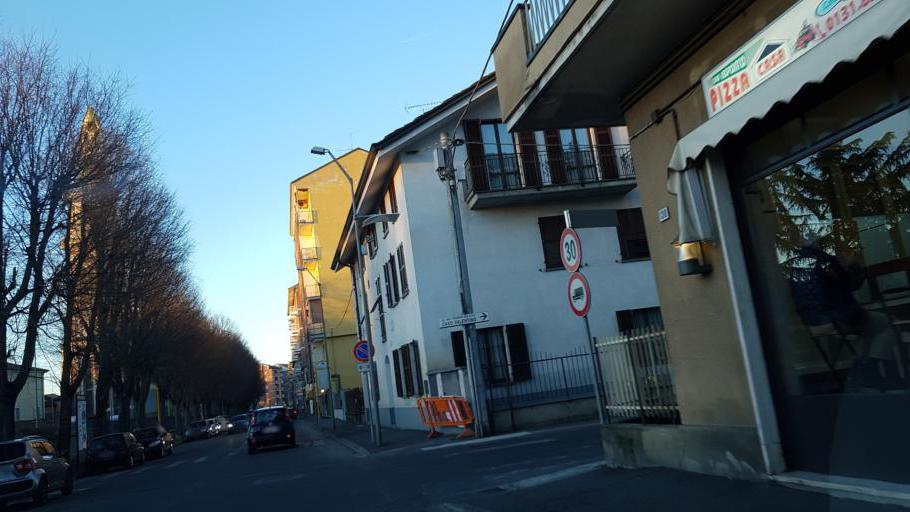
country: IT
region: Piedmont
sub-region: Provincia di Alessandria
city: Tortona
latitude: 44.8865
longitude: 8.8592
